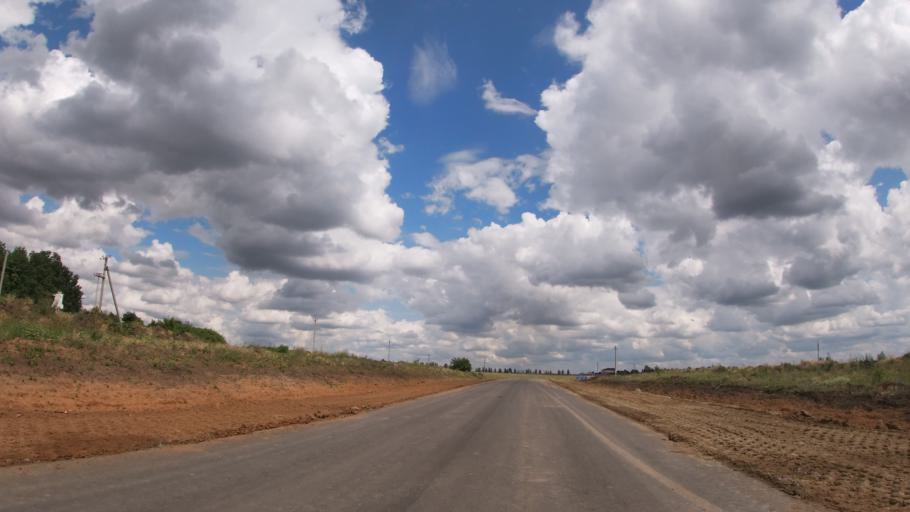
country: RU
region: Belgorod
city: Mayskiy
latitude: 50.5215
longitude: 36.5063
